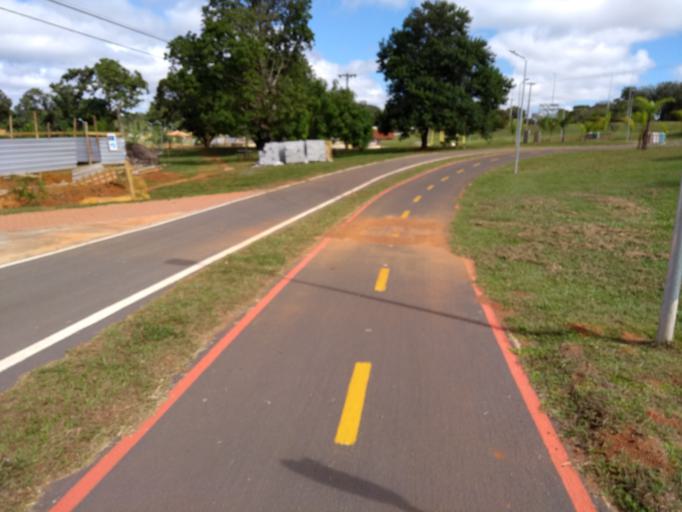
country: BR
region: Federal District
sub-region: Brasilia
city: Brasilia
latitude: -15.8373
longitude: -47.9007
